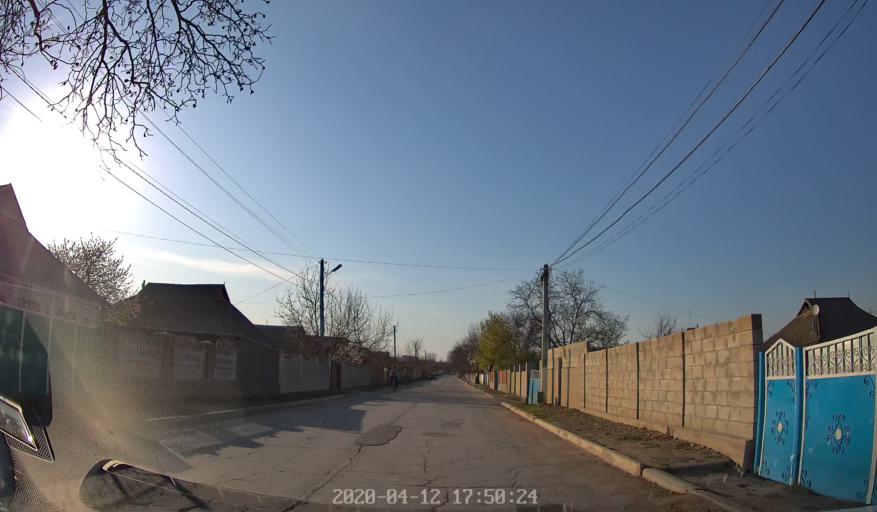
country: MD
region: Telenesti
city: Cocieri
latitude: 47.3760
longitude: 29.1272
